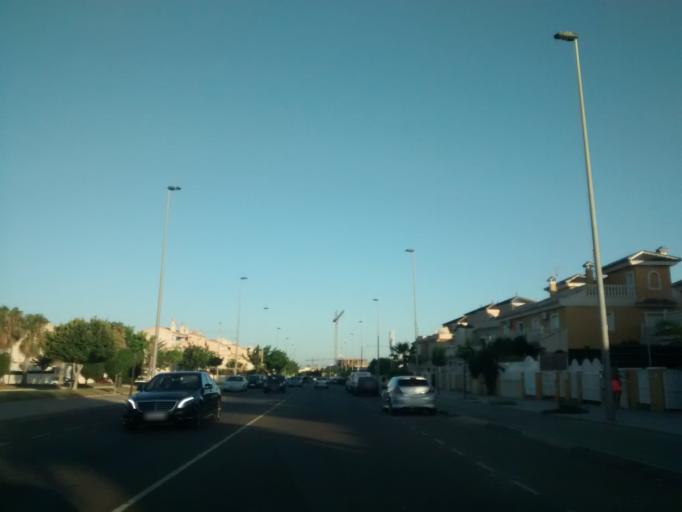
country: ES
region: Valencia
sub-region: Provincia de Alicante
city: Pilar de la Horadada
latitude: 37.8730
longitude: -0.7684
